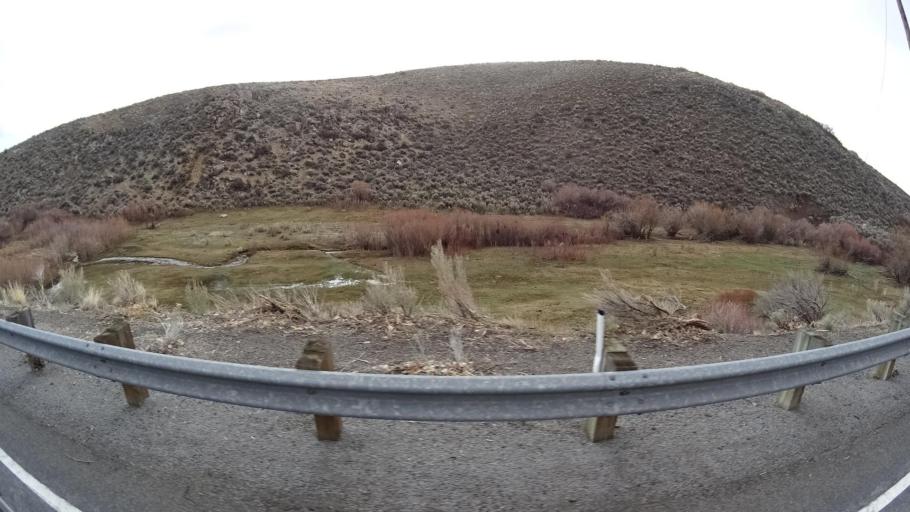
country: US
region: Nevada
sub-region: Washoe County
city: Cold Springs
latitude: 39.8320
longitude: -119.9377
